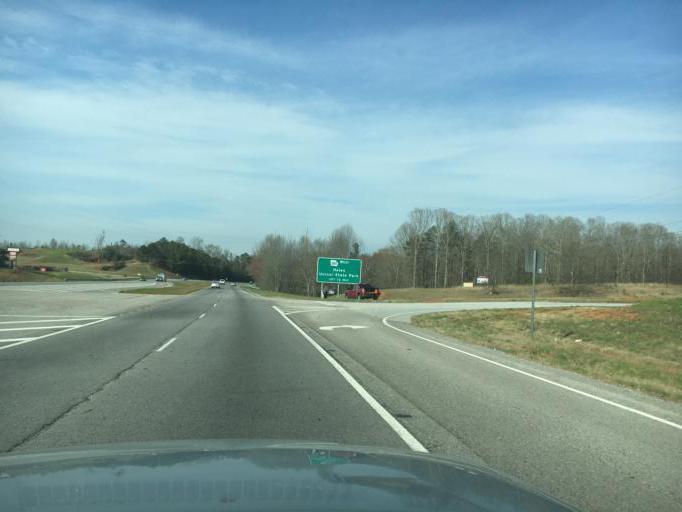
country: US
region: Georgia
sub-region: Banks County
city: Alto
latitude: 34.4902
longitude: -83.5797
